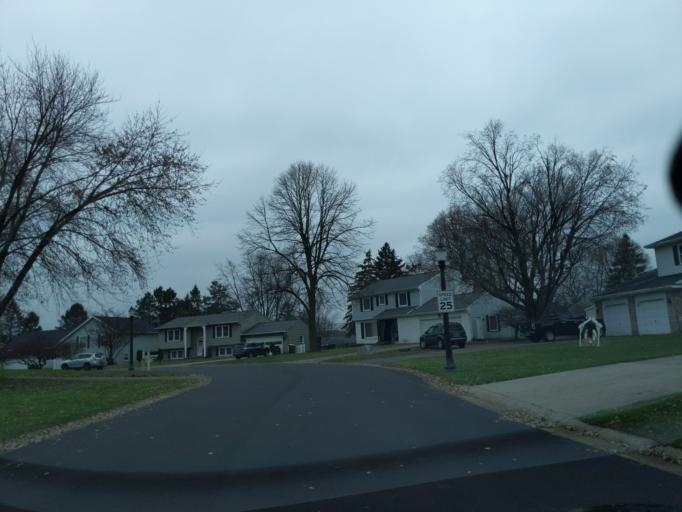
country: US
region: Michigan
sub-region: Eaton County
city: Waverly
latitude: 42.7320
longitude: -84.6300
